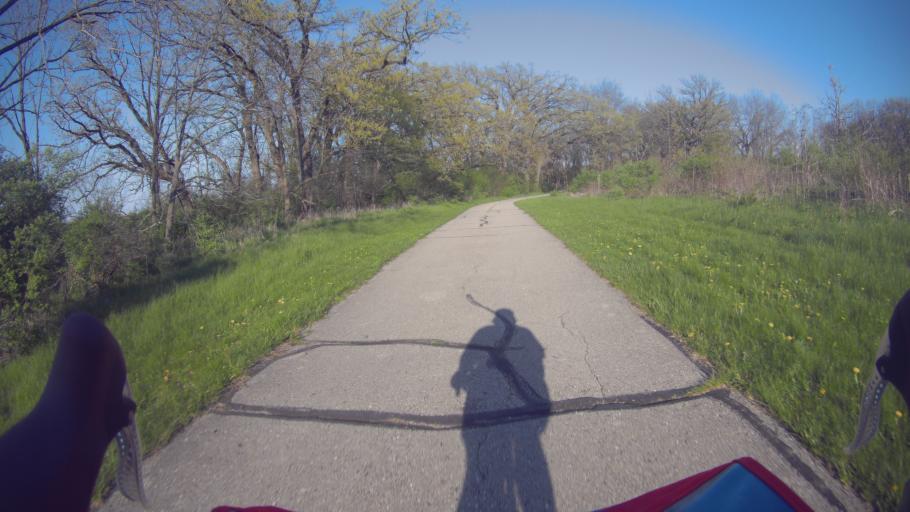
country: US
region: Wisconsin
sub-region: Dane County
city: Madison
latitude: 43.0103
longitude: -89.4187
